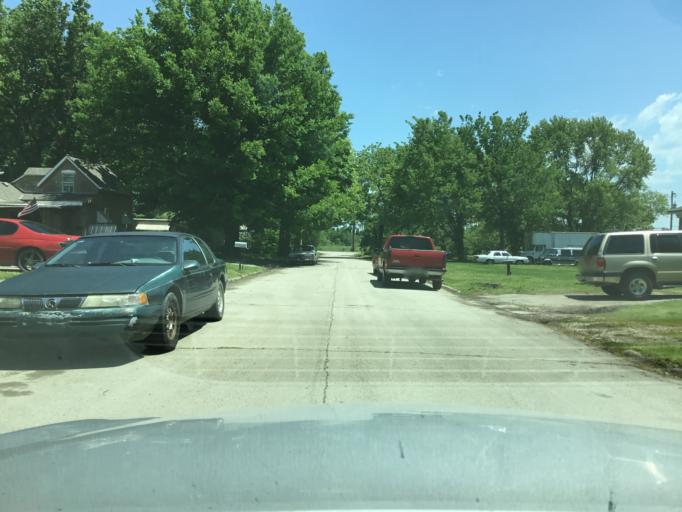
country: US
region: Kansas
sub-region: Montgomery County
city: Independence
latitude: 37.2188
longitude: -95.6945
